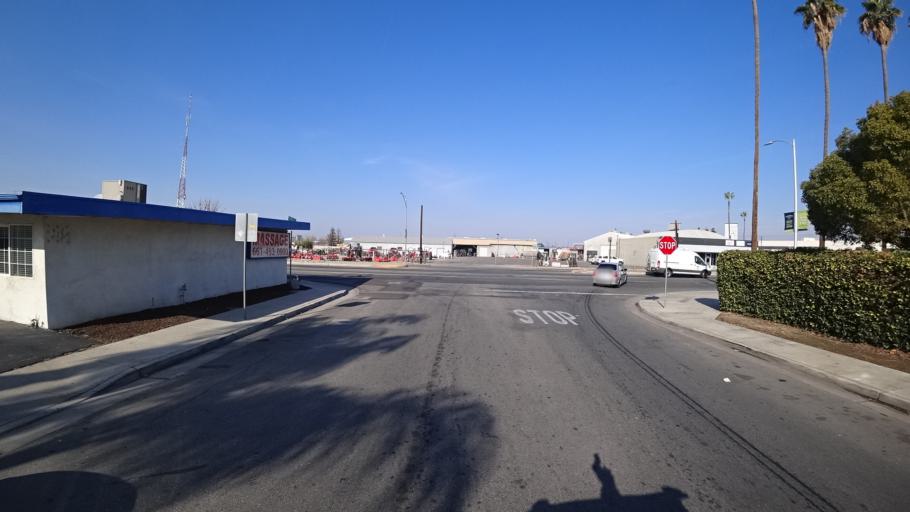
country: US
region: California
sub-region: Kern County
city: Bakersfield
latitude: 35.3681
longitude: -119.0043
